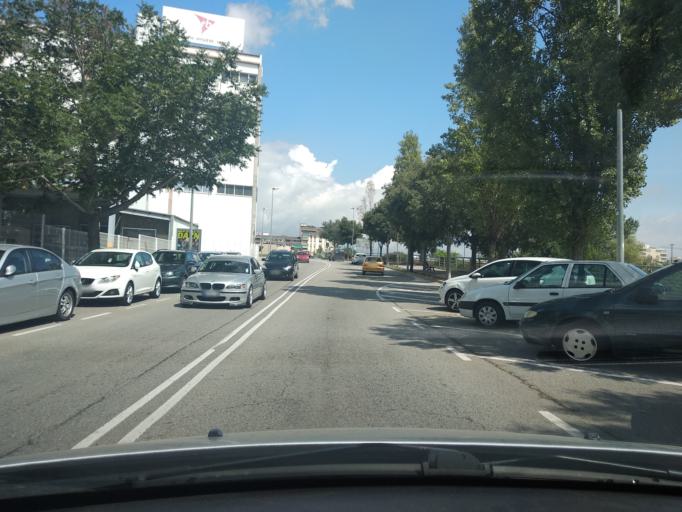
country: ES
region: Catalonia
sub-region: Provincia de Barcelona
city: Granollers
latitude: 41.6104
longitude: 2.2817
